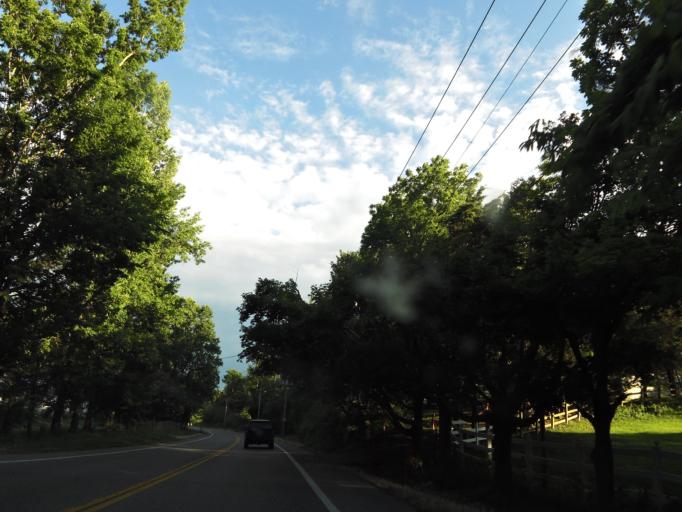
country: US
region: Missouri
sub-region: Saint Louis County
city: Wildwood
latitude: 38.6409
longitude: -90.6708
